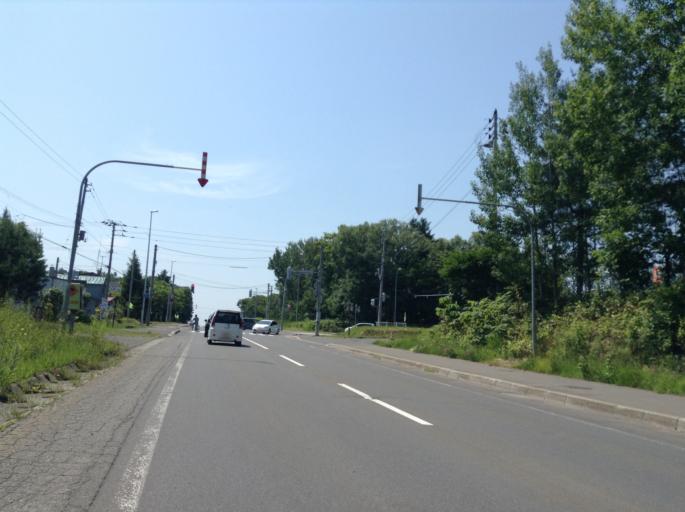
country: JP
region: Hokkaido
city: Nayoro
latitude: 44.3472
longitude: 142.4748
